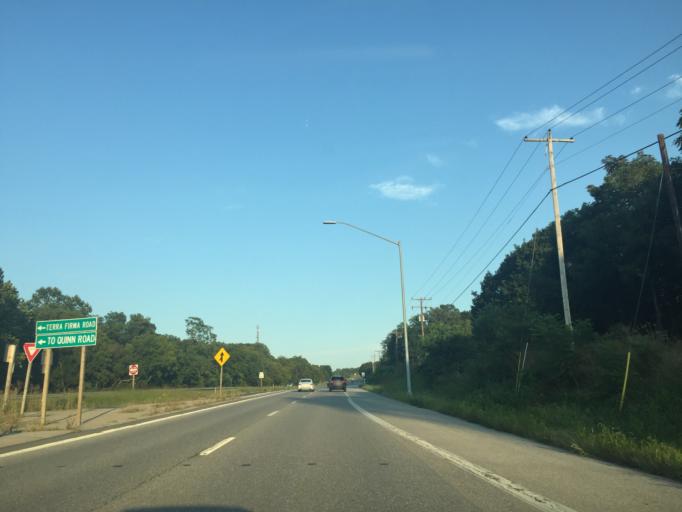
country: US
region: Maryland
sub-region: Frederick County
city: Spring Ridge
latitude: 39.3956
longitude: -77.3400
